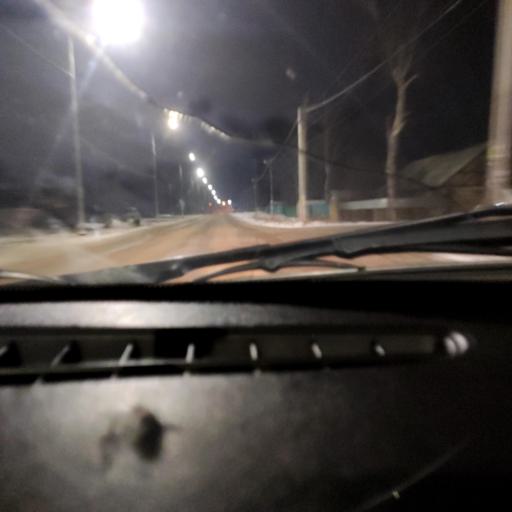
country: RU
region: Bashkortostan
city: Avdon
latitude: 54.6100
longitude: 55.8424
